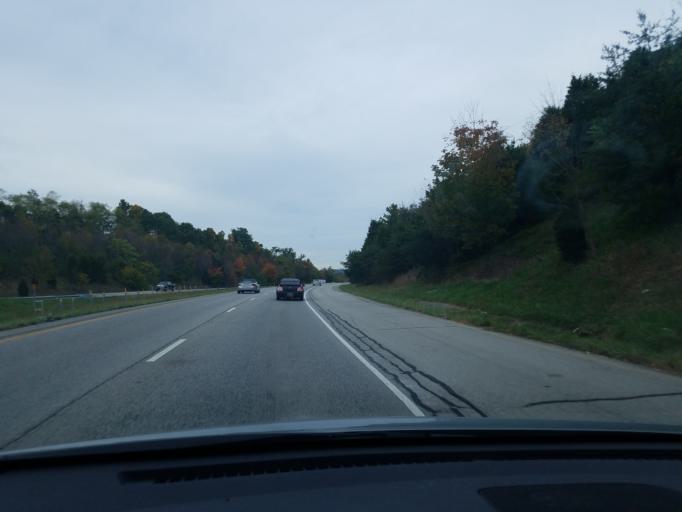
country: US
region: Indiana
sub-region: Floyd County
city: New Albany
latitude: 38.3059
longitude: -85.8497
